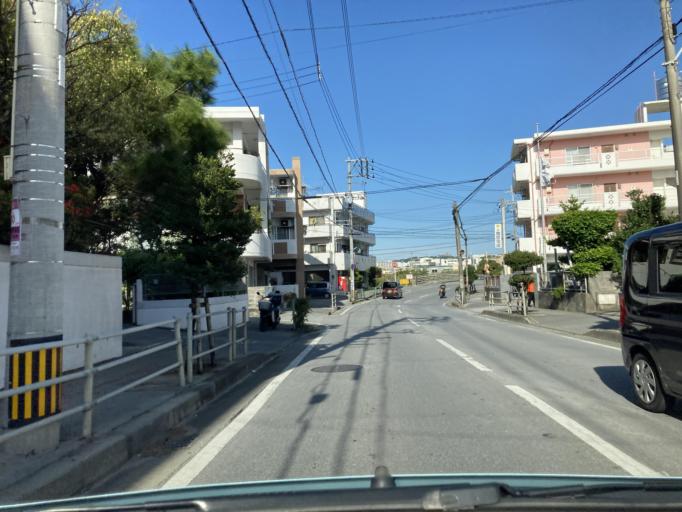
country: JP
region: Okinawa
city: Tomigusuku
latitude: 26.1863
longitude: 127.7082
